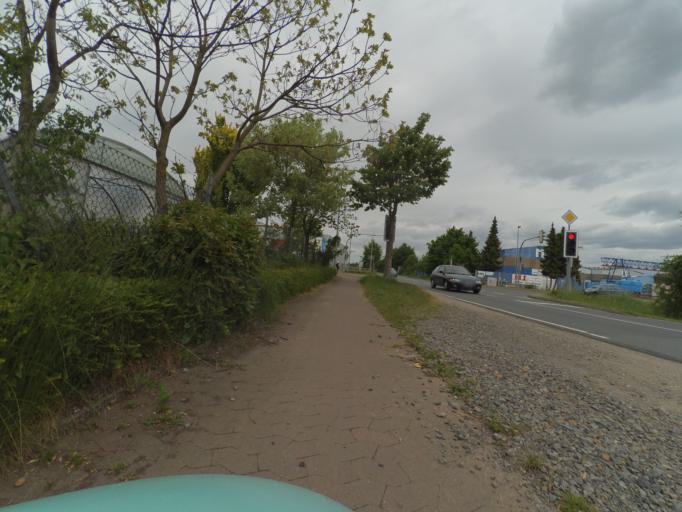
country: DE
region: Lower Saxony
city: Garbsen-Mitte
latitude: 52.4502
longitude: 9.5698
